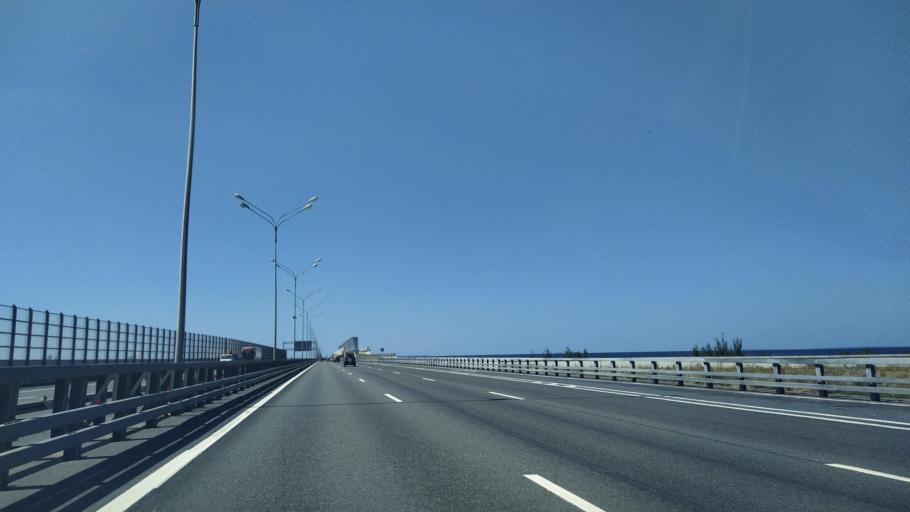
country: RU
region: Leningrad
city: Gorskaya
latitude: 60.0376
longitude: 29.9626
